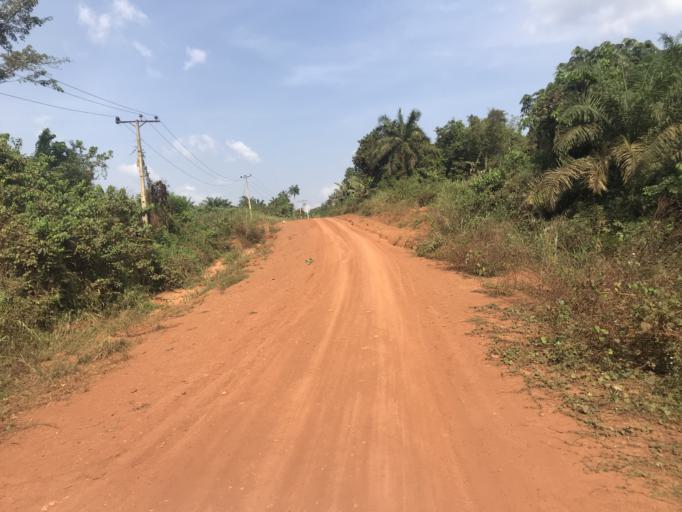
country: NG
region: Osun
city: Ilesa
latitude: 7.6544
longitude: 4.6675
